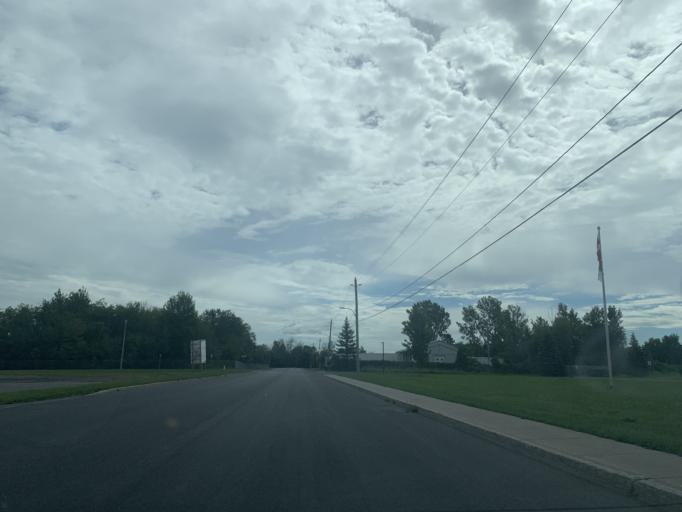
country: CA
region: Ontario
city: Hawkesbury
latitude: 45.6036
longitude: -74.5991
